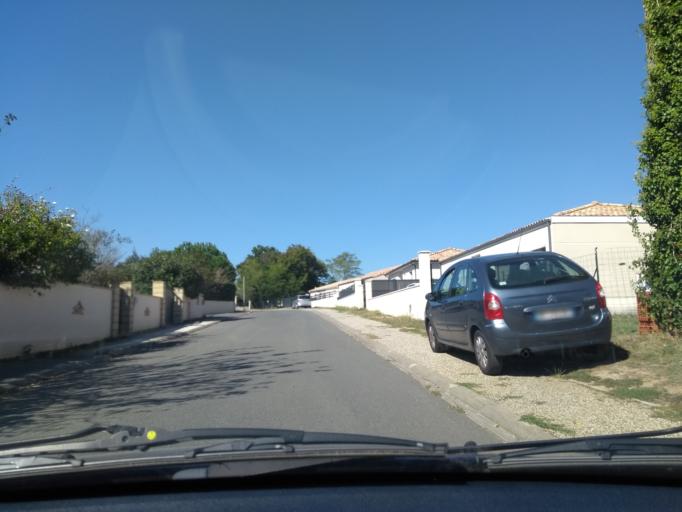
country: FR
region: Aquitaine
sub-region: Departement de la Gironde
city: Saucats
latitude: 44.6504
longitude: -0.5990
